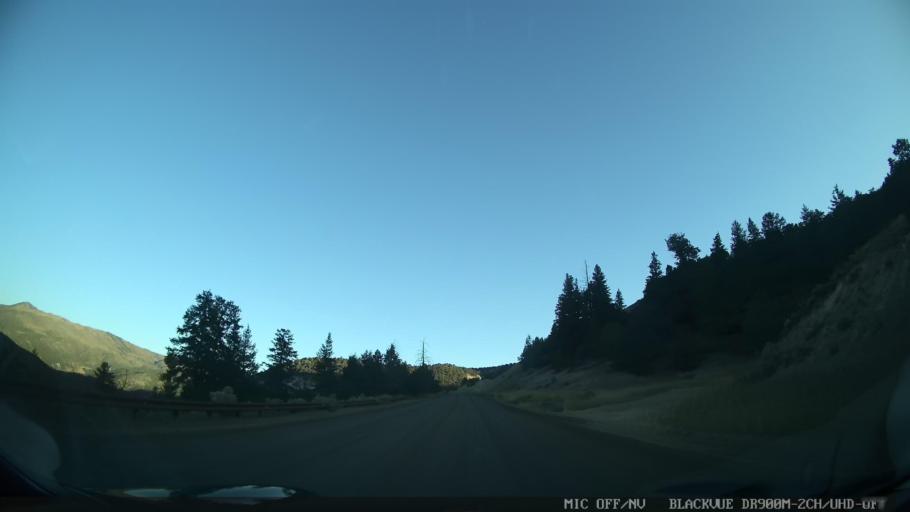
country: US
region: Colorado
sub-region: Grand County
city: Kremmling
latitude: 39.9432
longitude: -106.5284
